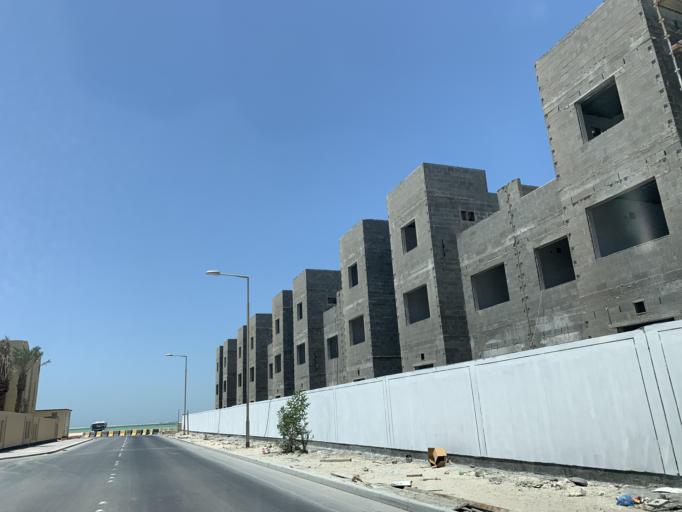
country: BH
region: Manama
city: Jidd Hafs
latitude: 26.2342
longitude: 50.4917
